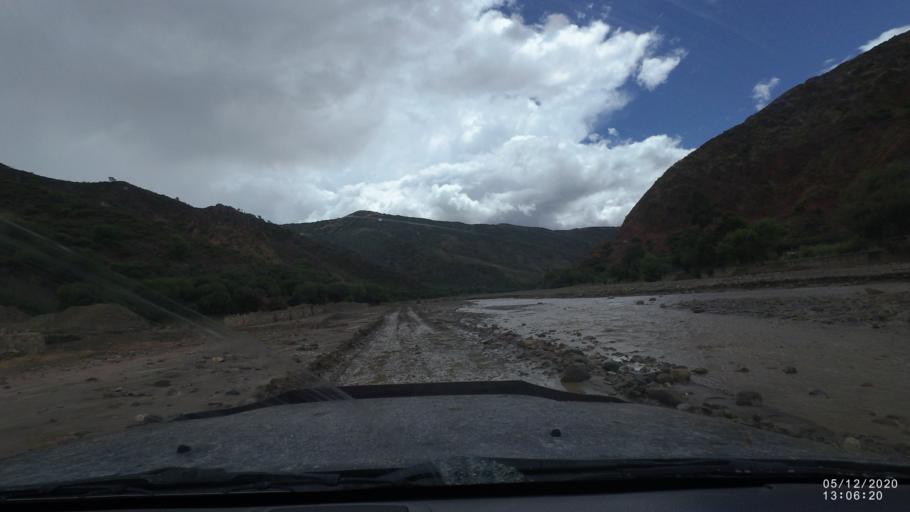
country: BO
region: Cochabamba
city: Sipe Sipe
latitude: -17.5578
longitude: -66.4445
